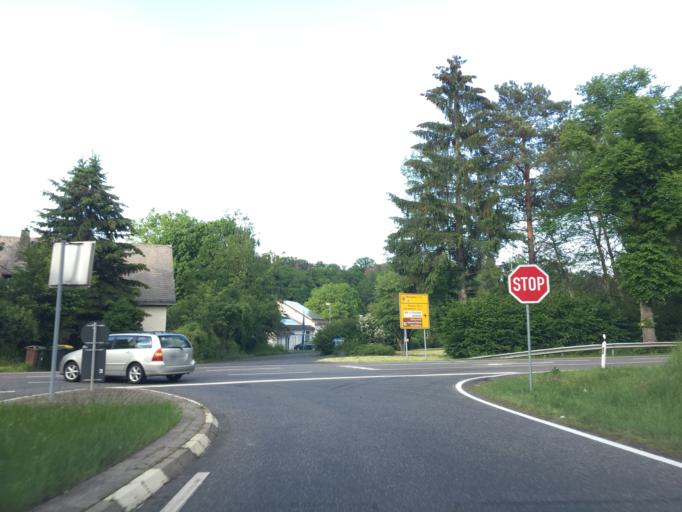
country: DE
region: Rheinland-Pfalz
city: Holler
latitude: 50.4297
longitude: 7.8420
